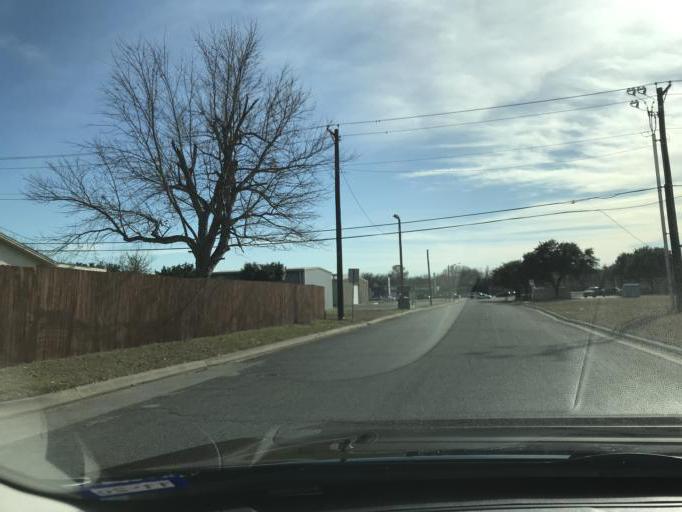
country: US
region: Texas
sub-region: Denton County
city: Denton
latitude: 33.2312
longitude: -97.1516
